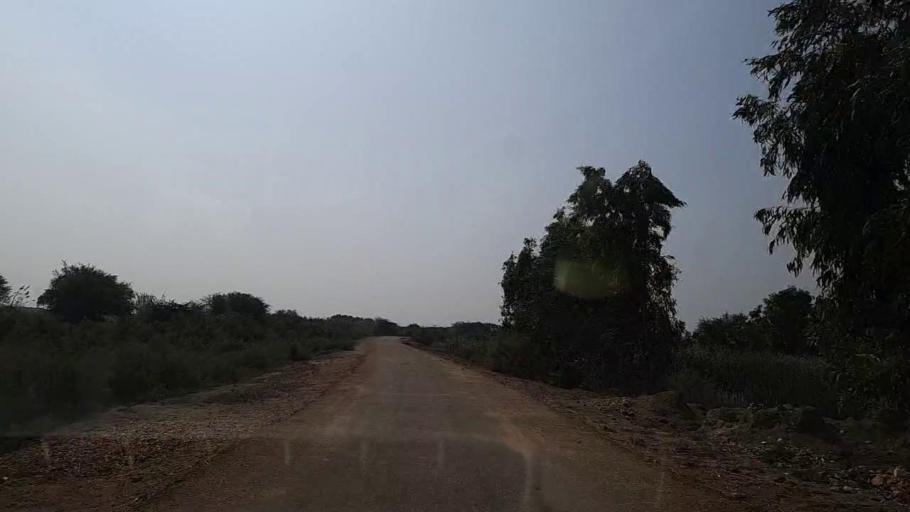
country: PK
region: Sindh
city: Mirpur Sakro
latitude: 24.5267
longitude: 67.7750
